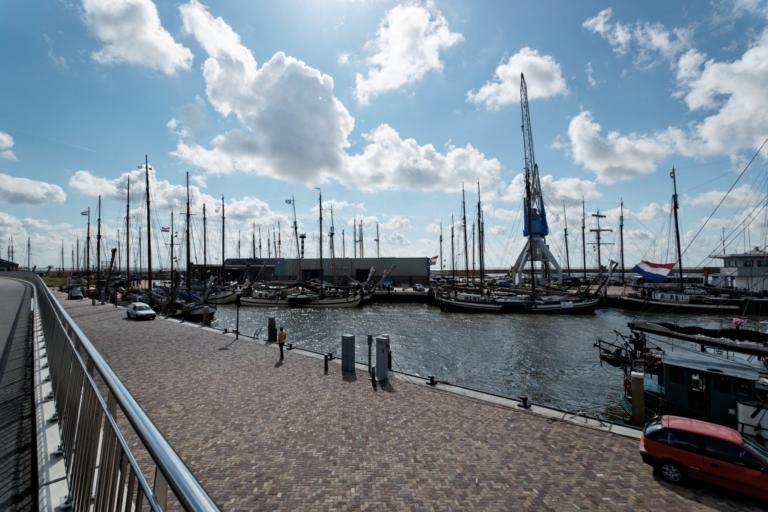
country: NL
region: Friesland
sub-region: Gemeente Harlingen
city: Harlingen
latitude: 53.1745
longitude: 5.4114
